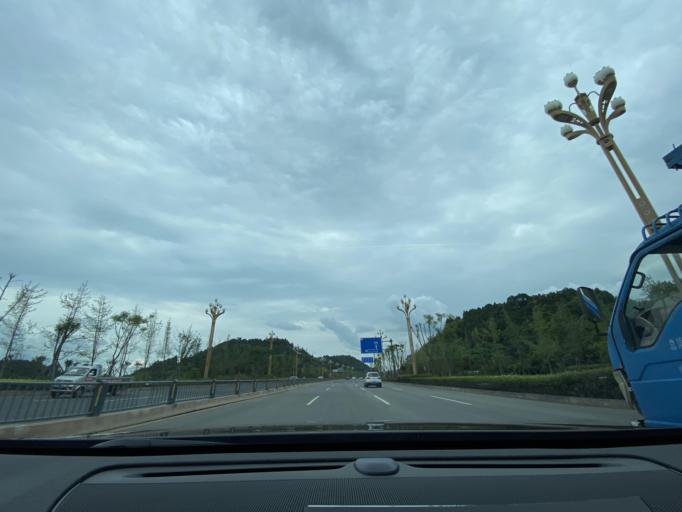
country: CN
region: Sichuan
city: Jiancheng
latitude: 30.4692
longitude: 104.4939
